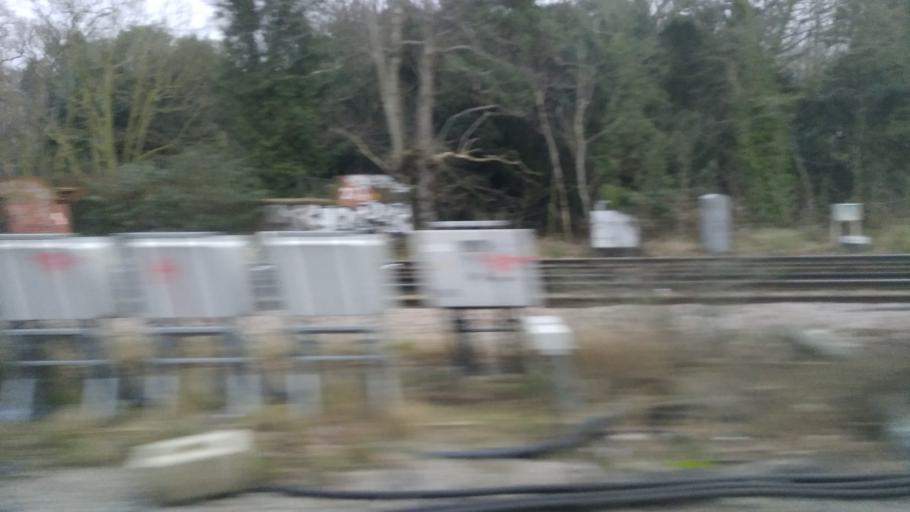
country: GB
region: England
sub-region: Greater London
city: Chislehurst
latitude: 51.4045
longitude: 0.0586
